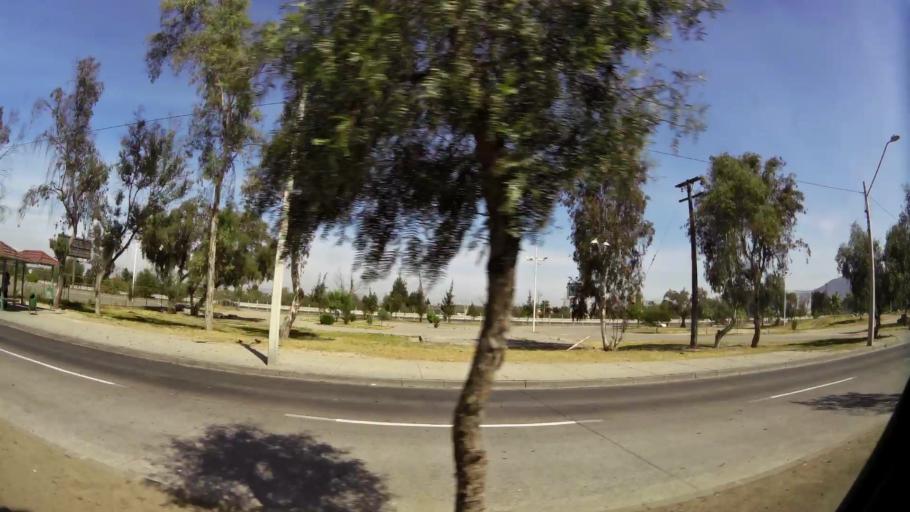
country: CL
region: Santiago Metropolitan
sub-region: Provincia de Santiago
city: Lo Prado
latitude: -33.4476
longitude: -70.7649
